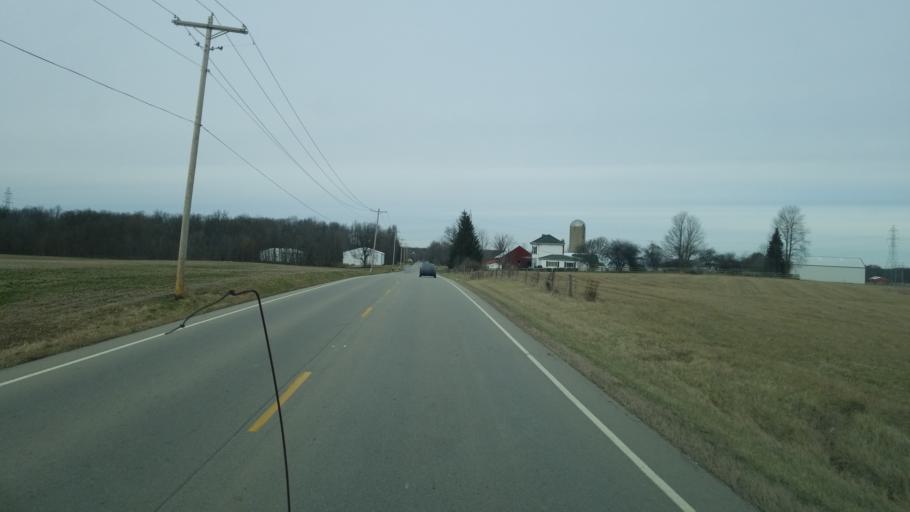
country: US
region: Ohio
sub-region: Adams County
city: Winchester
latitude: 39.0252
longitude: -83.7051
